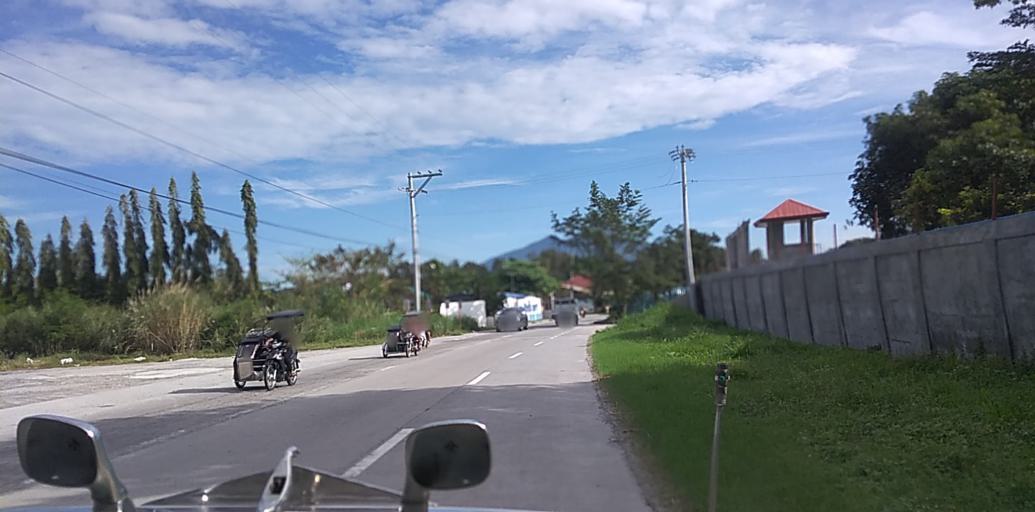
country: PH
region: Central Luzon
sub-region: Province of Pampanga
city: Malino
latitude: 15.1241
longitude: 120.6683
